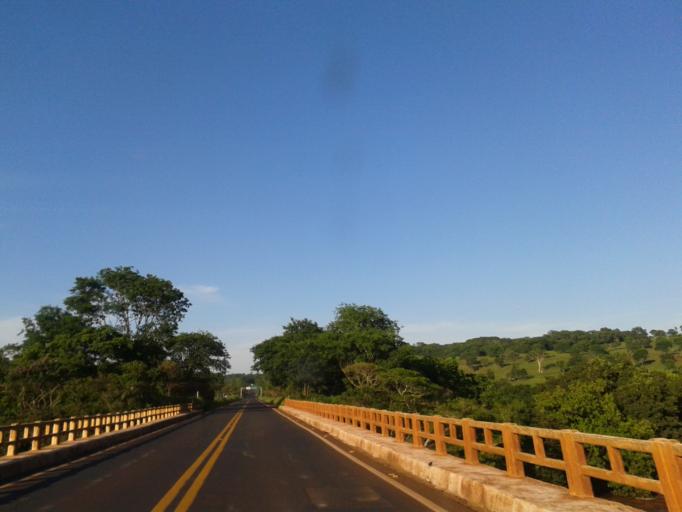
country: BR
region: Minas Gerais
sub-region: Santa Vitoria
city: Santa Vitoria
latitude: -18.9352
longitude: -49.7992
